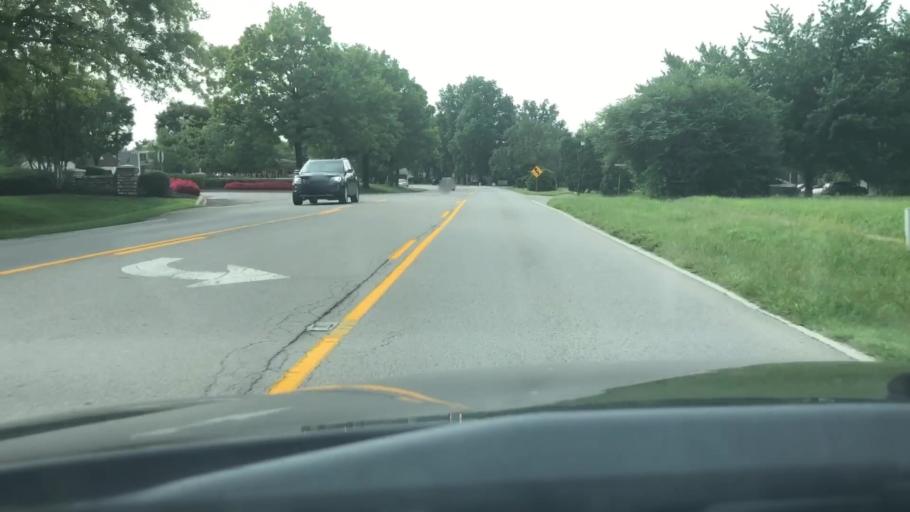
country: US
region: Kentucky
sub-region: Jefferson County
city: Graymoor-Devondale
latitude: 38.2672
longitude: -85.6130
